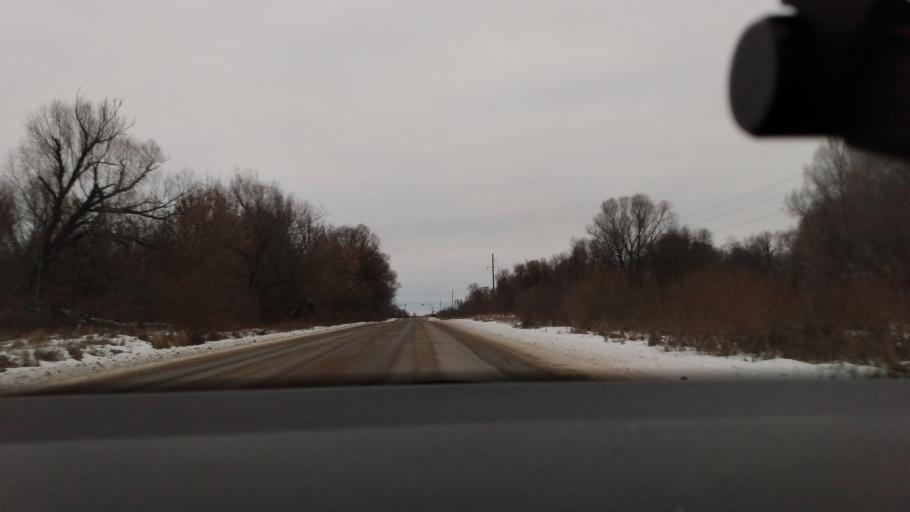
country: RU
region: Moskovskaya
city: Krasnaya Poyma
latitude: 55.0973
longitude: 39.1466
